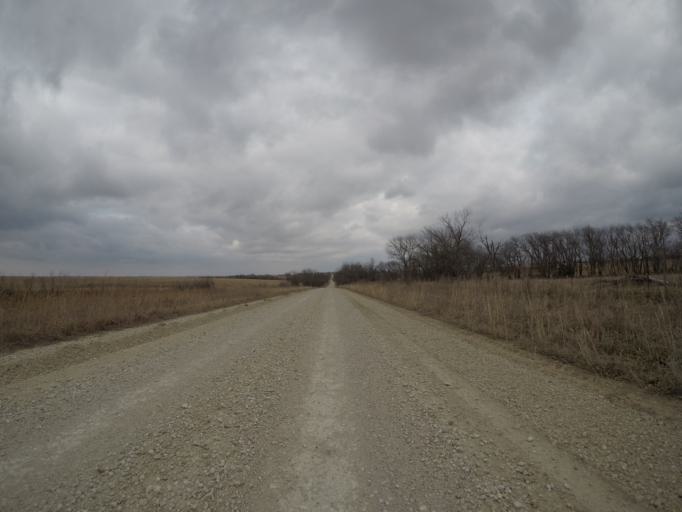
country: US
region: Kansas
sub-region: Morris County
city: Council Grove
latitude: 38.7296
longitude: -96.2796
